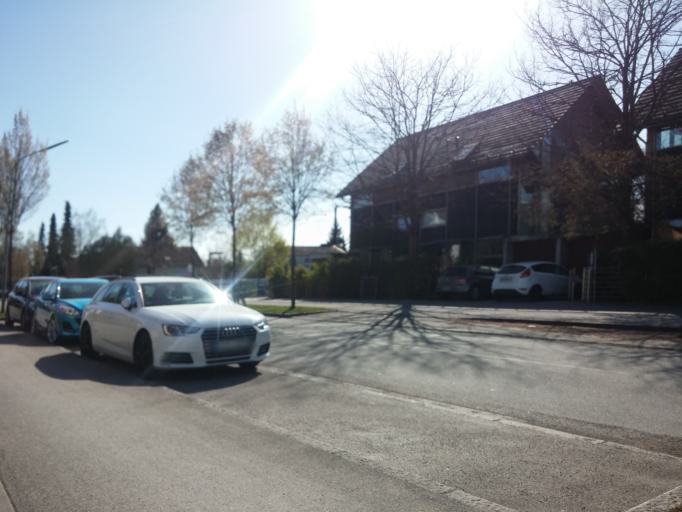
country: DE
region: Bavaria
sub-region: Upper Bavaria
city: Neubiberg
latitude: 48.0835
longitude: 11.6611
